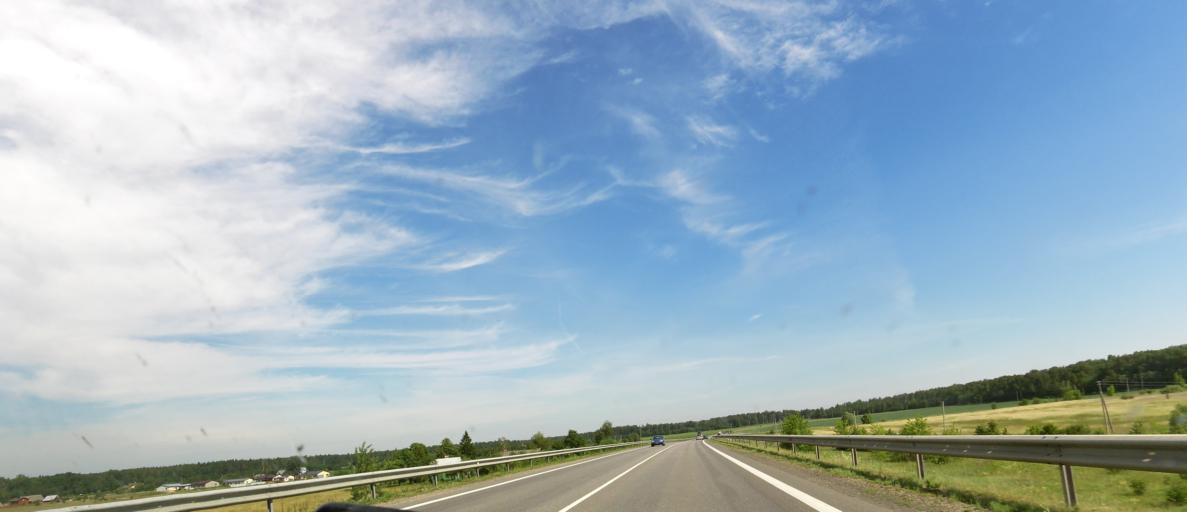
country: LT
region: Panevezys
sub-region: Panevezys City
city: Panevezys
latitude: 55.7468
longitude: 24.2773
